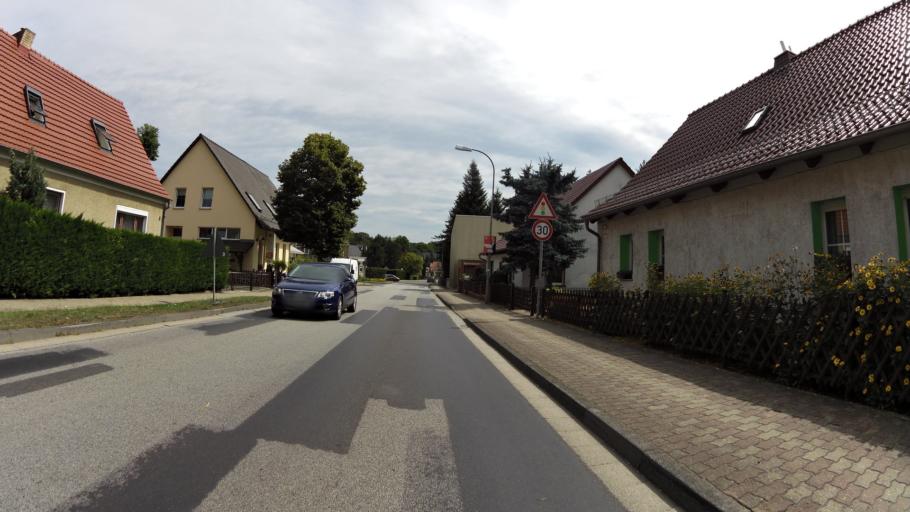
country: DE
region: Brandenburg
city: Neuzelle
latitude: 52.0866
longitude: 14.6446
